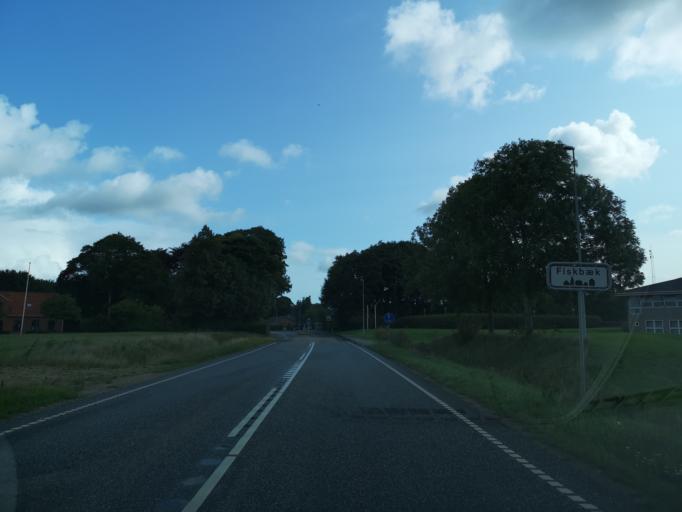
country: DK
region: Central Jutland
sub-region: Ringkobing-Skjern Kommune
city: Videbaek
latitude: 56.0434
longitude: 8.6189
